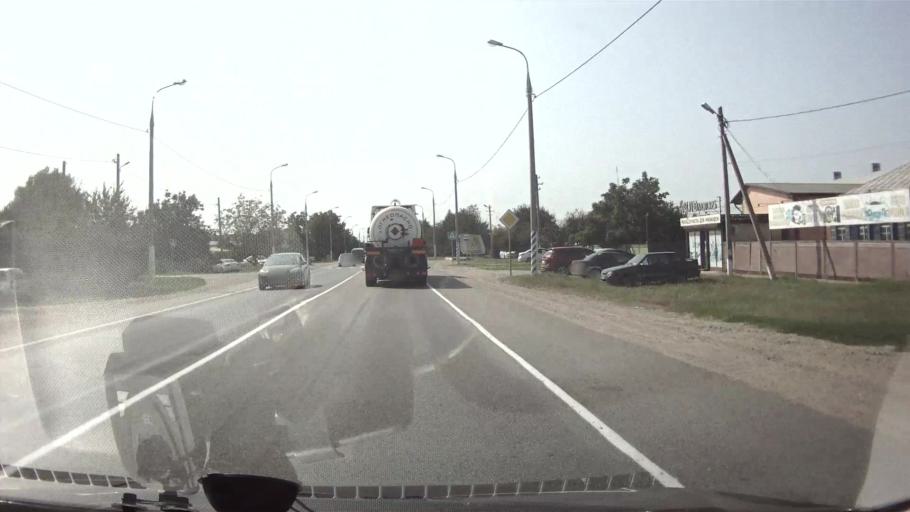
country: RU
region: Adygeya
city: Krasnogvardeyskoye
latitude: 45.2157
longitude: 39.5577
